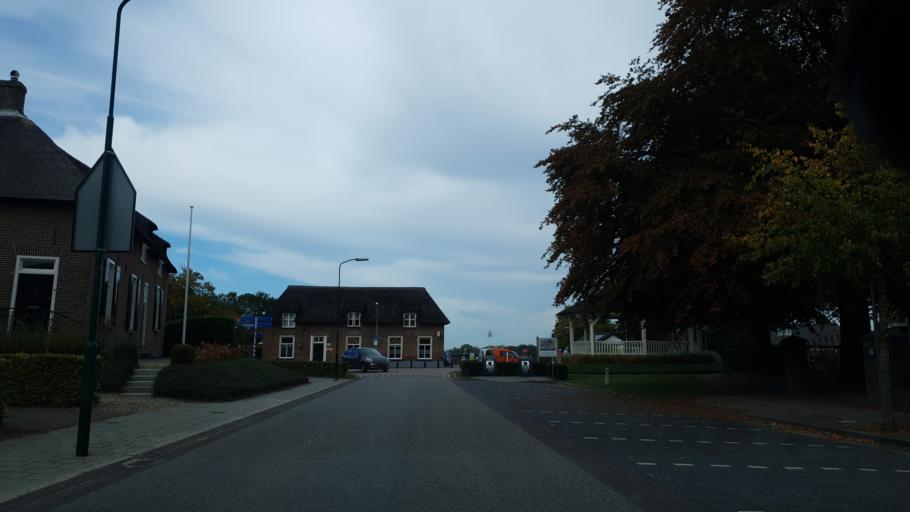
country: NL
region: Gelderland
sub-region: Gemeente Wijchen
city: Bergharen
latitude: 51.8508
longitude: 5.6656
